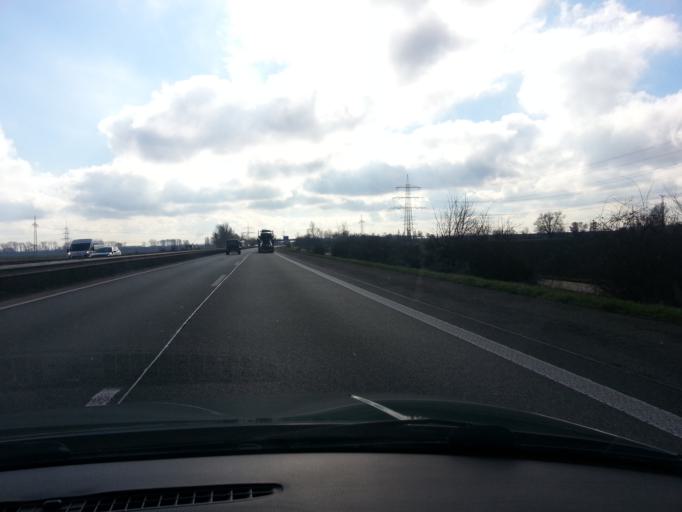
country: DE
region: Rheinland-Pfalz
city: Mutterstadt
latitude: 49.4217
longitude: 8.3380
